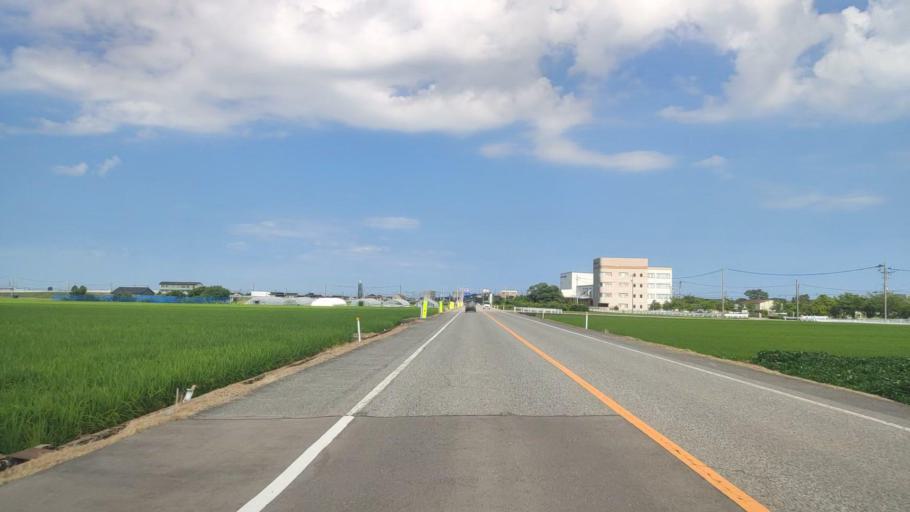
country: JP
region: Ishikawa
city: Matsuto
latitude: 36.4673
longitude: 136.5839
